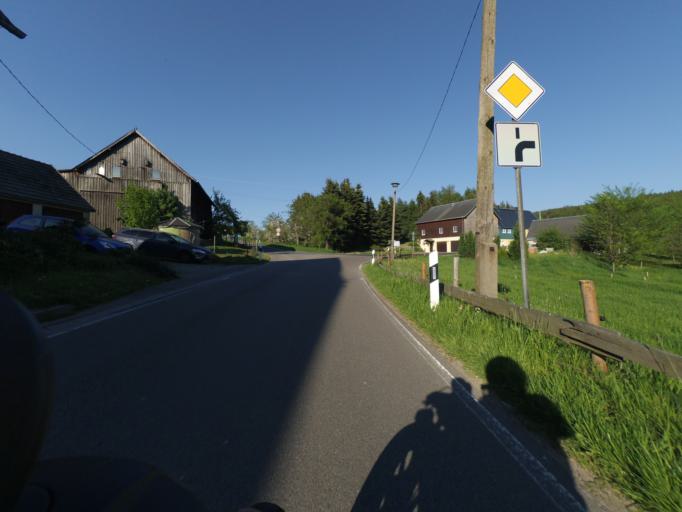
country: DE
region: Saxony
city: Frauenstein
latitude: 50.8272
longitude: 13.5690
